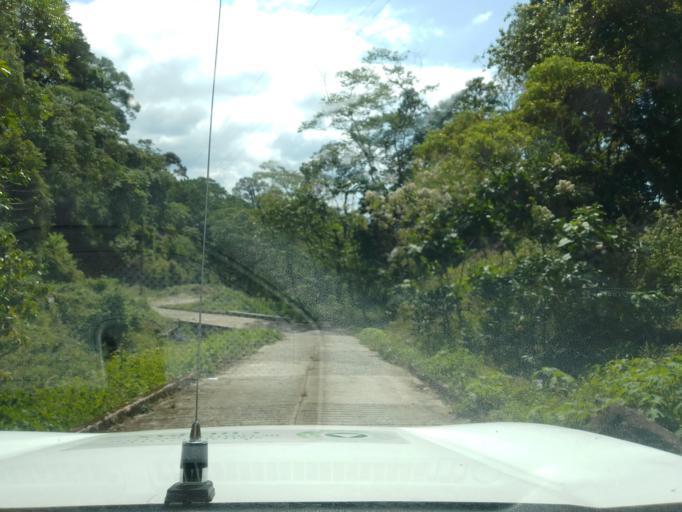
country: MX
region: Chiapas
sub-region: Union Juarez
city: Santo Domingo
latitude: 15.0726
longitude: -92.0922
